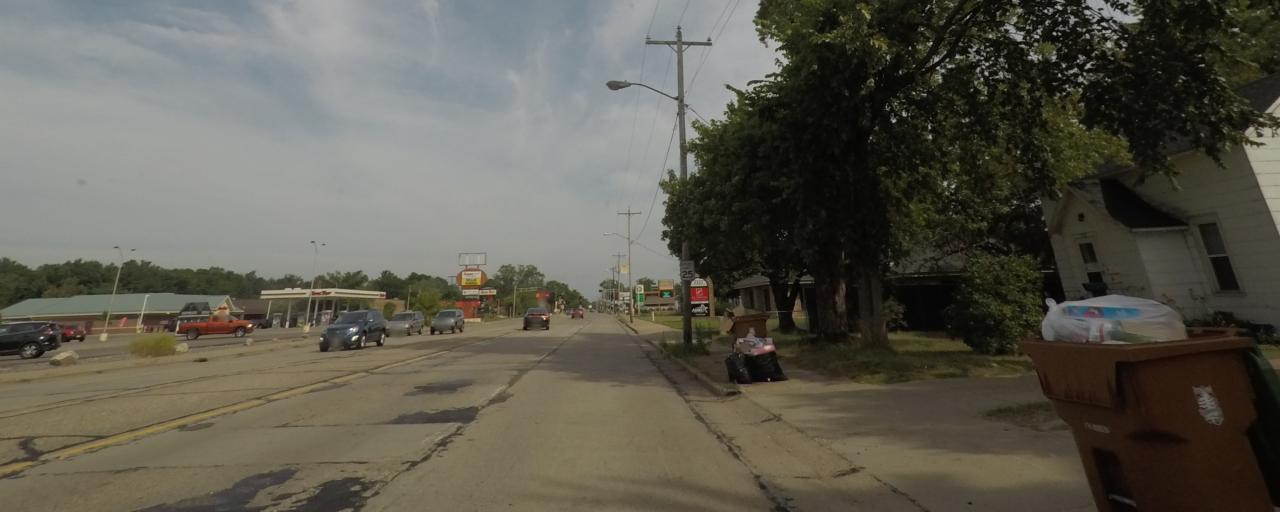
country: US
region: Wisconsin
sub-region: Portage County
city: Whiting
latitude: 44.5032
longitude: -89.5657
